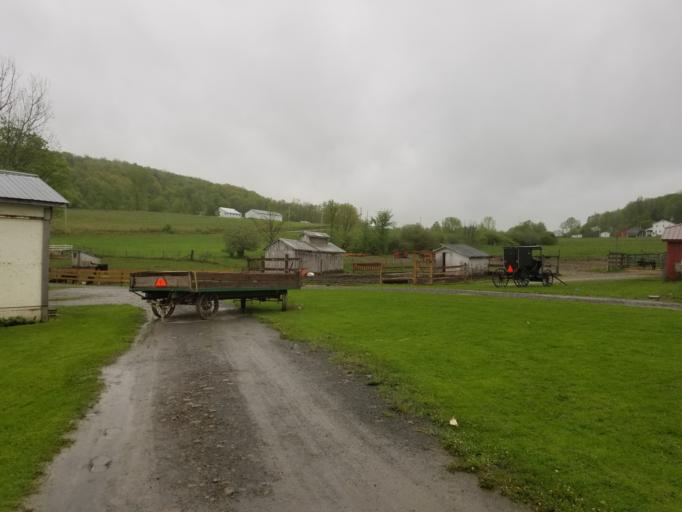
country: US
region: Pennsylvania
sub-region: Tioga County
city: Westfield
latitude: 42.0421
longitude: -77.4646
